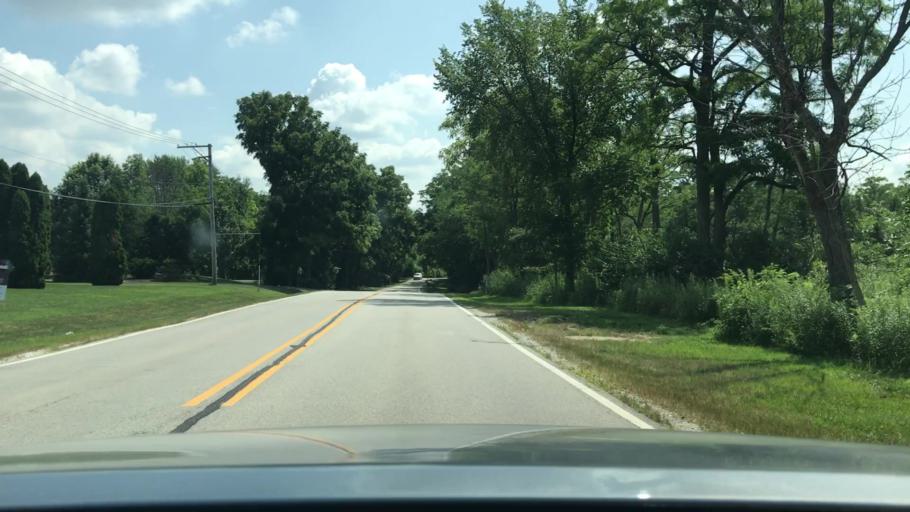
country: US
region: Illinois
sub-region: DuPage County
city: Darien
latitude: 41.7293
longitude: -88.0079
